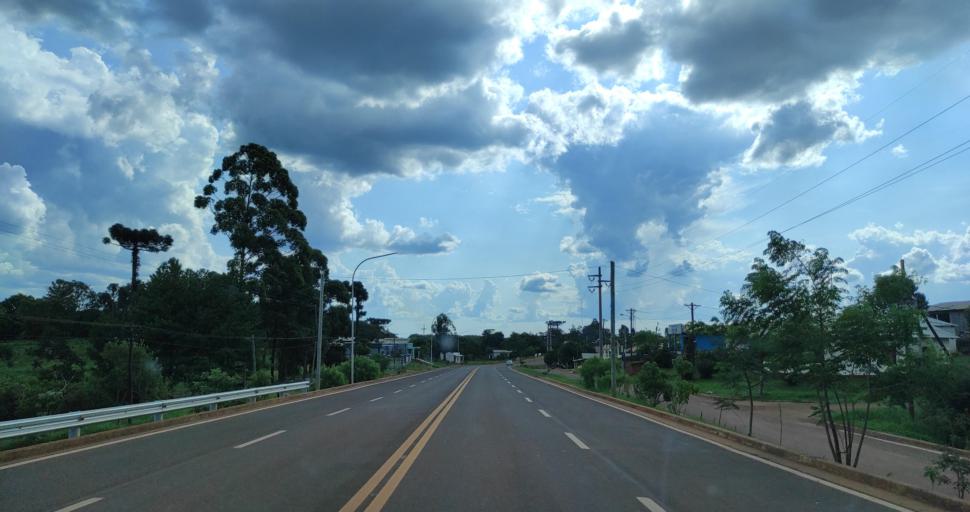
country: AR
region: Misiones
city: Bernardo de Irigoyen
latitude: -26.2948
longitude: -53.7468
